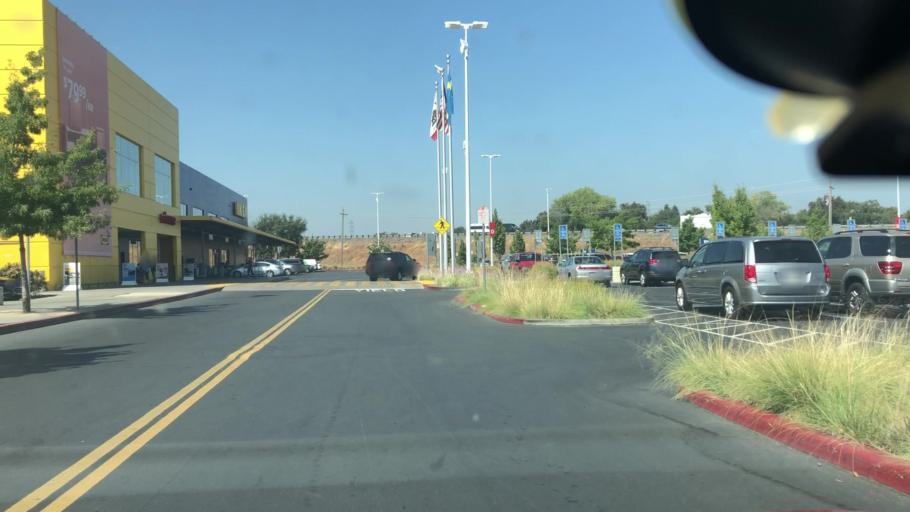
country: US
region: California
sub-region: Yolo County
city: West Sacramento
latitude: 38.5874
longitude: -121.5530
